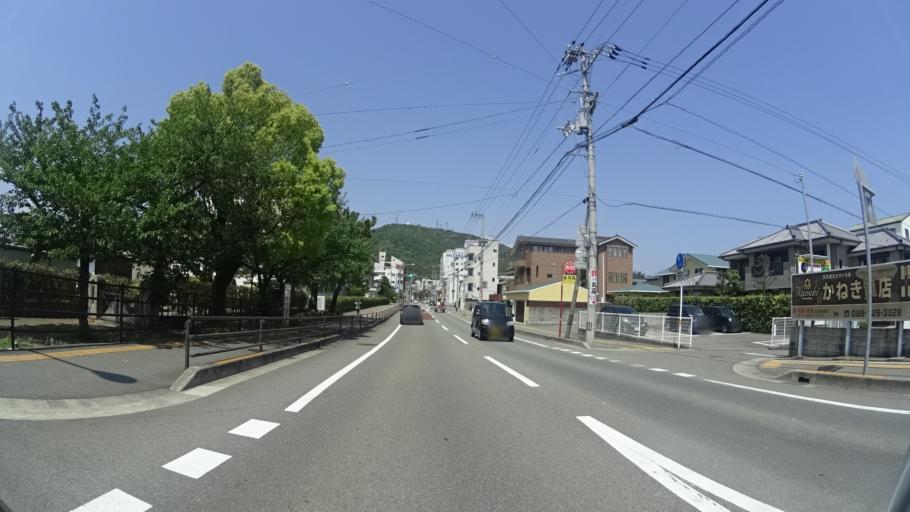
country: JP
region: Tokushima
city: Tokushima-shi
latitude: 34.0622
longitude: 134.5546
